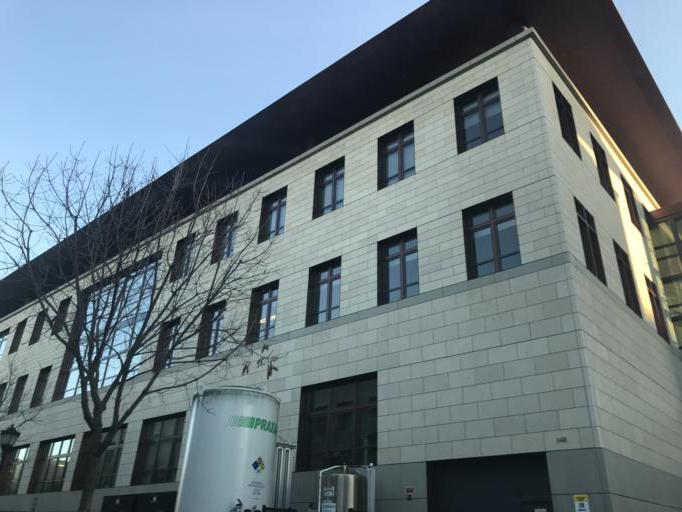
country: US
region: California
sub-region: Santa Clara County
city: Stanford
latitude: 37.4291
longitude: -122.1744
